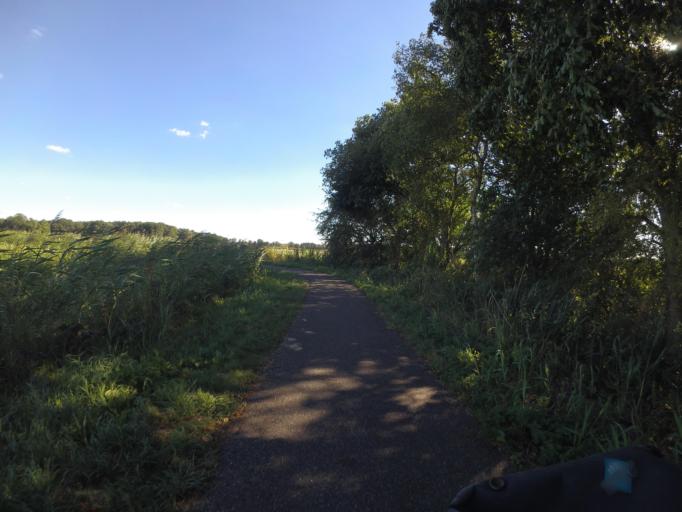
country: NL
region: Drenthe
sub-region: Gemeente Aa en Hunze
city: Anloo
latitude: 52.9944
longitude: 6.6708
